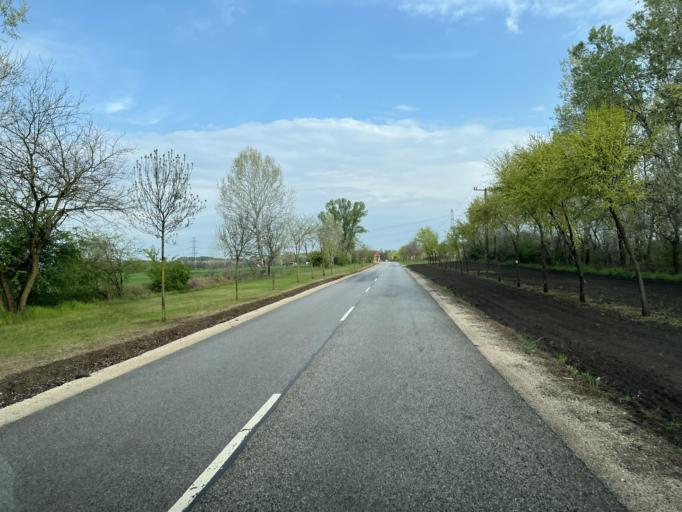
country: HU
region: Pest
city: Ujhartyan
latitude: 47.2380
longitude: 19.4432
